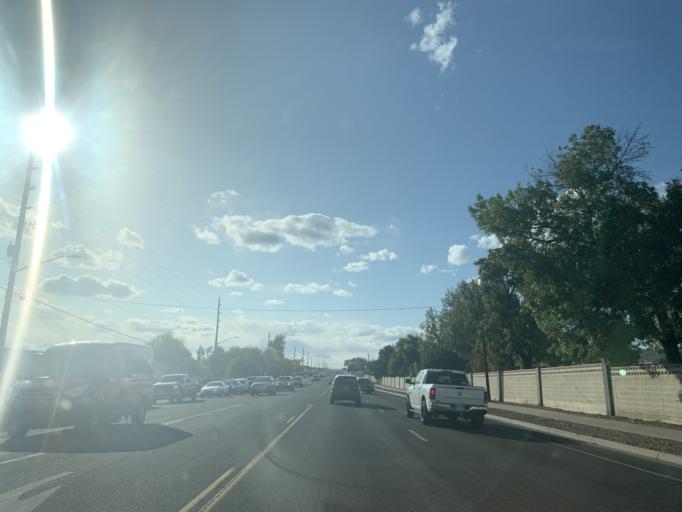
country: US
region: Colorado
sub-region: Mesa County
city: Fruitvale
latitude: 39.0919
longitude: -108.5171
